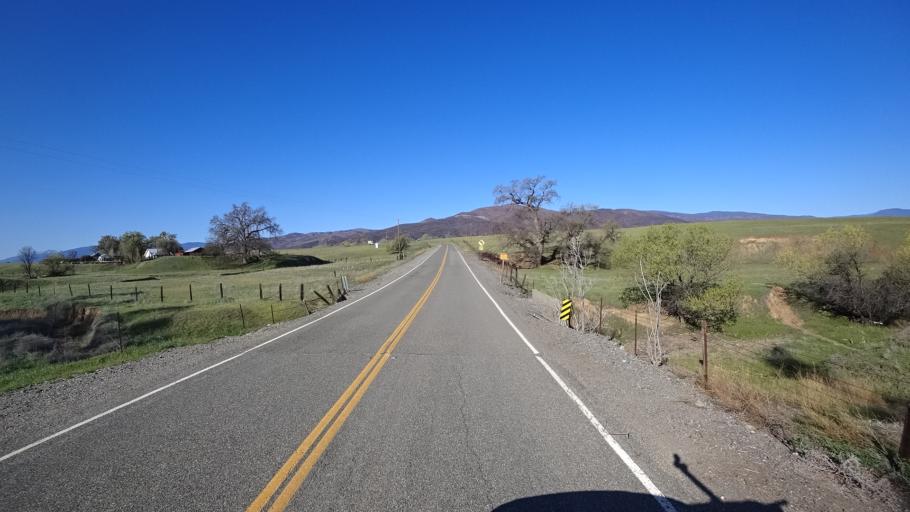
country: US
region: California
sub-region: Tehama County
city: Rancho Tehama Reserve
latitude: 39.7466
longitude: -122.5374
